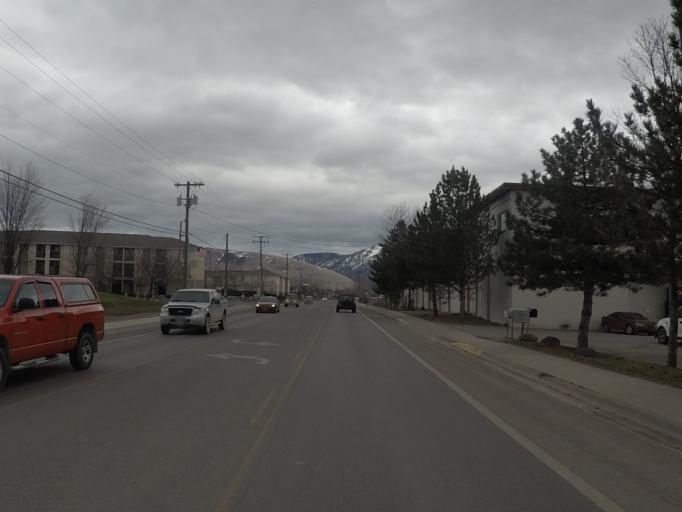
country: US
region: Montana
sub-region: Missoula County
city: Orchard Homes
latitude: 46.8844
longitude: -114.0368
